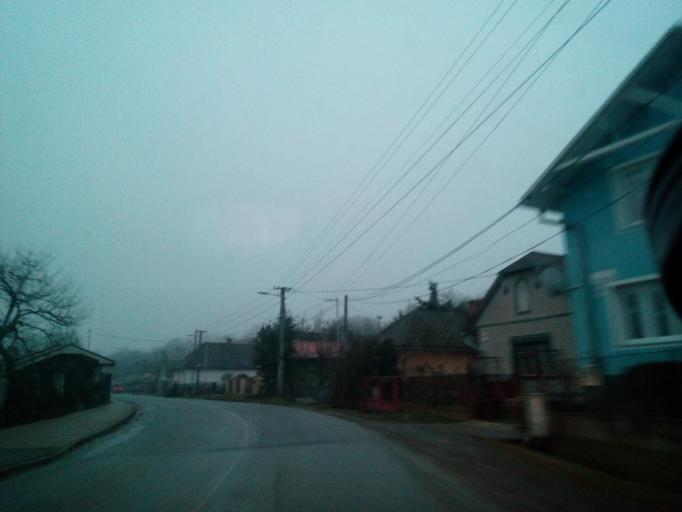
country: SK
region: Presovsky
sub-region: Okres Presov
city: Presov
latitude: 49.0380
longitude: 21.1921
